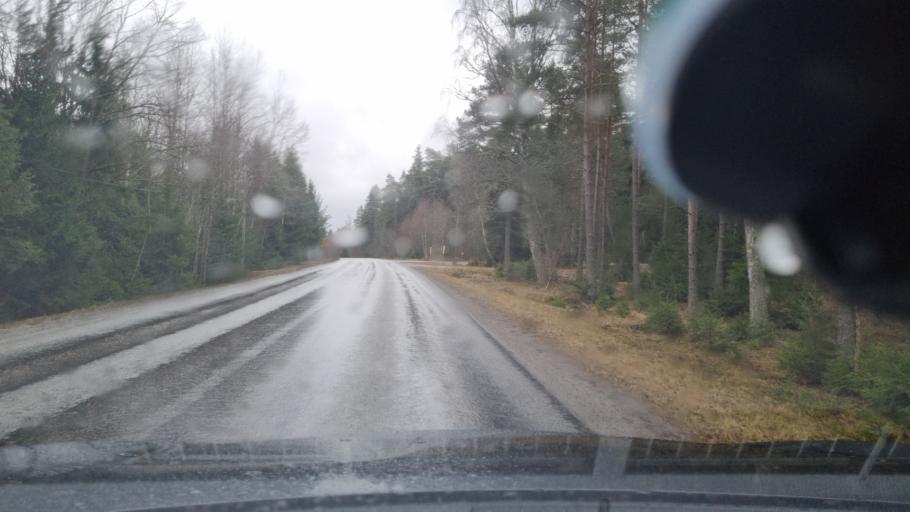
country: SE
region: Stockholm
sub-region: Upplands-Bro Kommun
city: Kungsaengen
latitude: 59.5411
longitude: 17.7405
